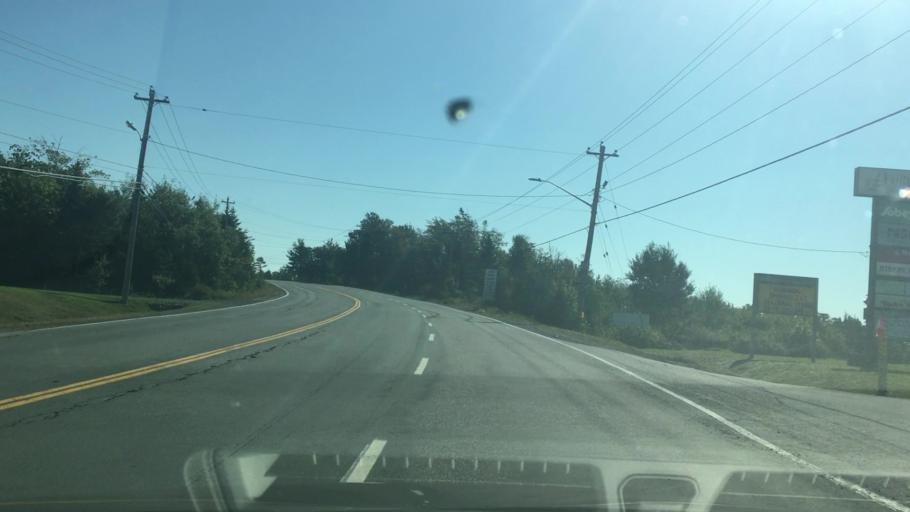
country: CA
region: Nova Scotia
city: Cole Harbour
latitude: 44.7783
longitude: -63.0910
